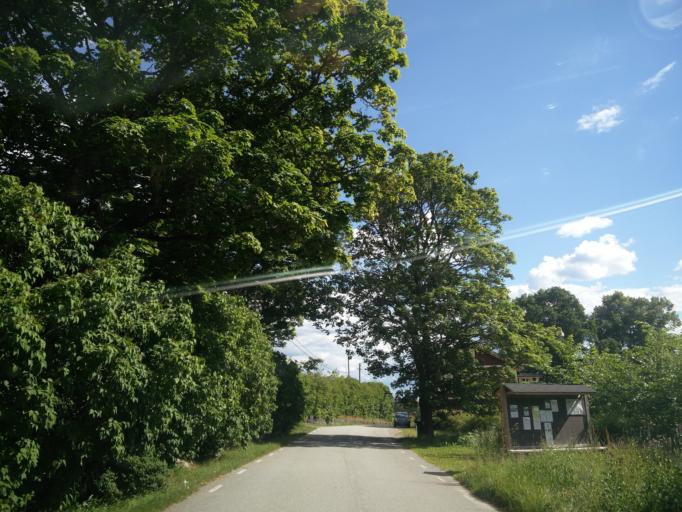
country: SE
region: OErebro
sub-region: Ljusnarsbergs Kommun
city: Kopparberg
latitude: 59.7835
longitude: 14.7790
